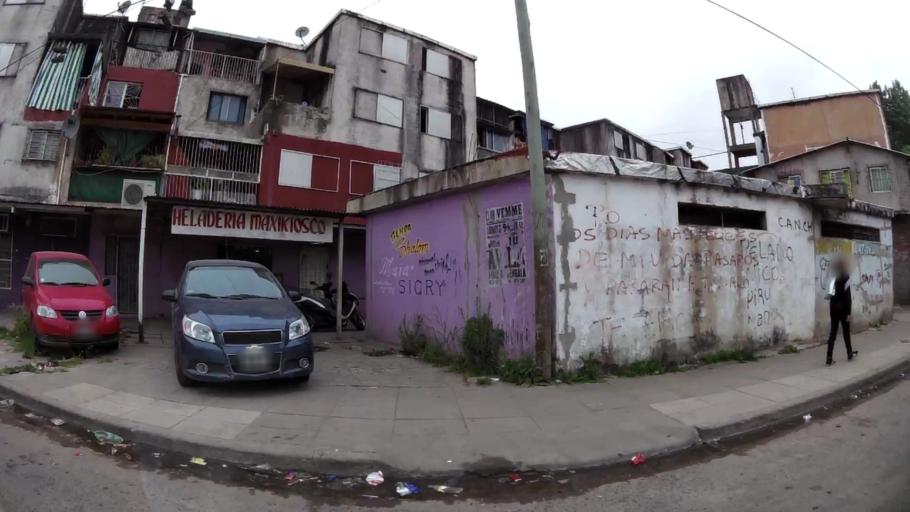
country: AR
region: Buenos Aires
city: San Justo
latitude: -34.7038
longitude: -58.5401
